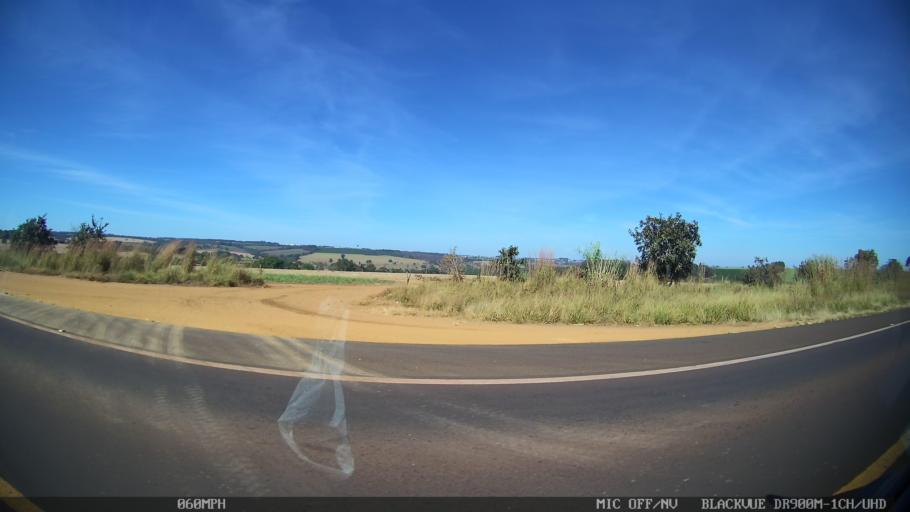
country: BR
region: Sao Paulo
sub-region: Franca
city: Franca
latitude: -20.5542
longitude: -47.4929
